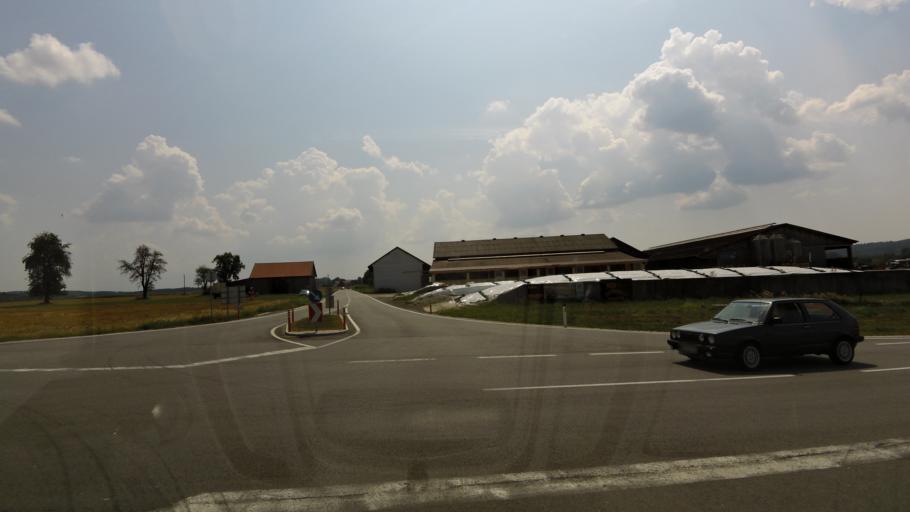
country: AT
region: Upper Austria
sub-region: Politischer Bezirk Ried im Innkreis
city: Waldzell
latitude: 48.1778
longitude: 13.4050
